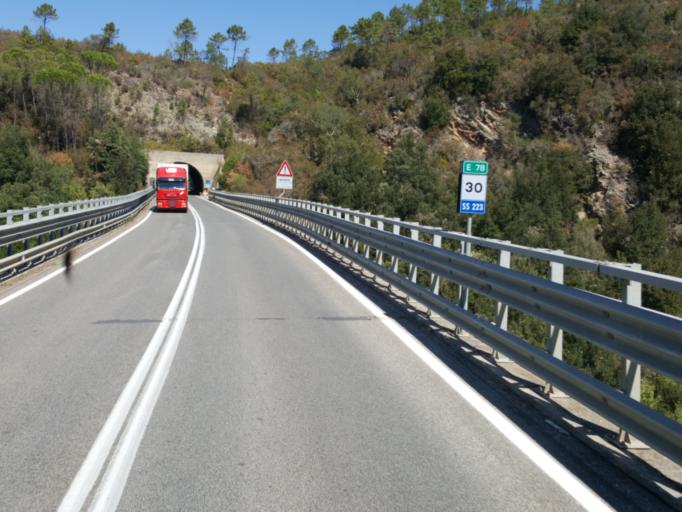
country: IT
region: Tuscany
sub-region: Provincia di Grosseto
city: Civitella Marittima
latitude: 43.0148
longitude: 11.2878
